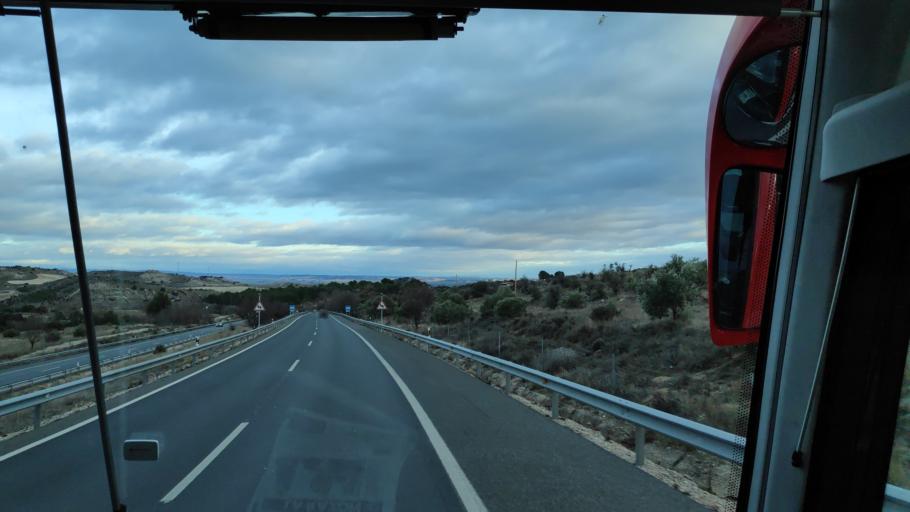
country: ES
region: Madrid
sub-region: Provincia de Madrid
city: Villarejo de Salvanes
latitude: 40.1493
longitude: -3.2317
